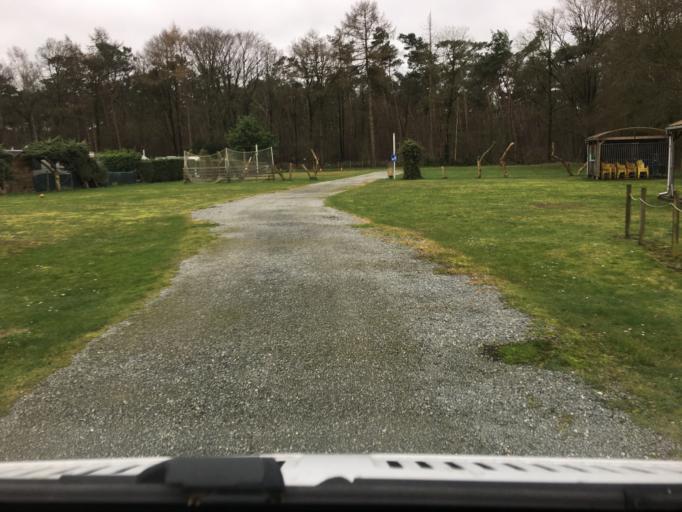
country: BE
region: Flanders
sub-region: Provincie Oost-Vlaanderen
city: Kaprijke
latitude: 51.1807
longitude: 3.6419
